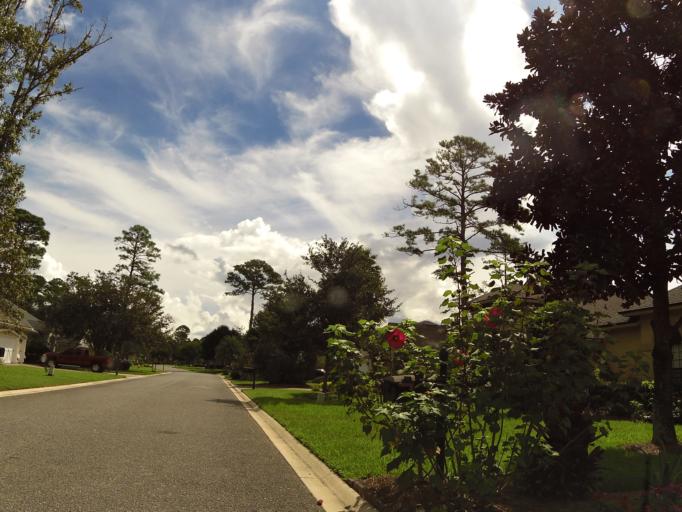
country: US
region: Florida
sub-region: Nassau County
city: Fernandina Beach
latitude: 30.6256
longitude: -81.4644
